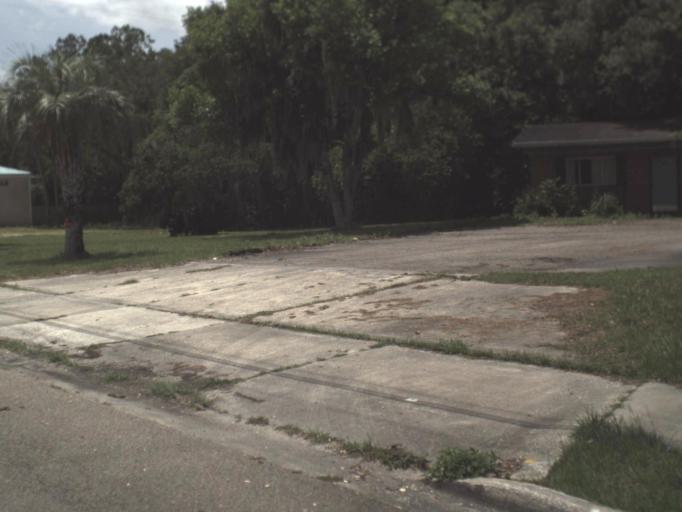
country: US
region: Florida
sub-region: Taylor County
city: Perry
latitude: 30.0960
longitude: -83.5811
